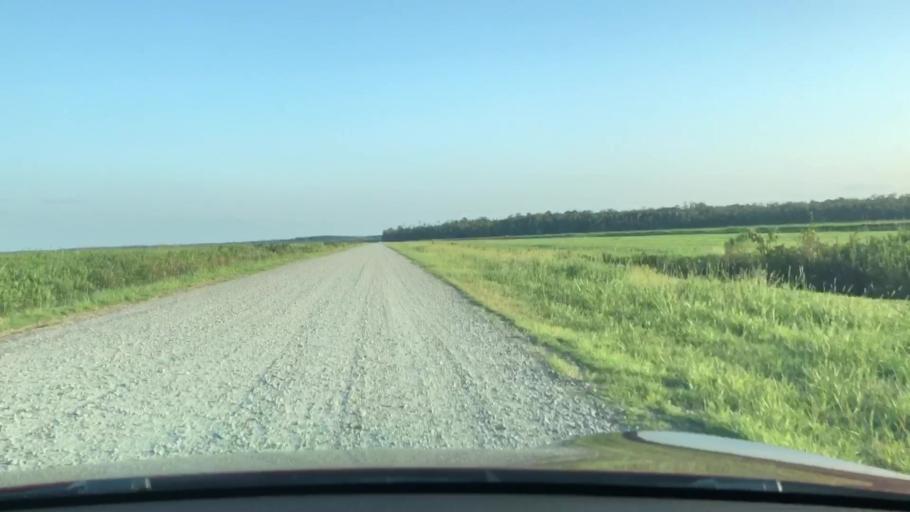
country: US
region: North Carolina
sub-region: Dare County
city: Manteo
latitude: 35.8534
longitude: -75.8621
